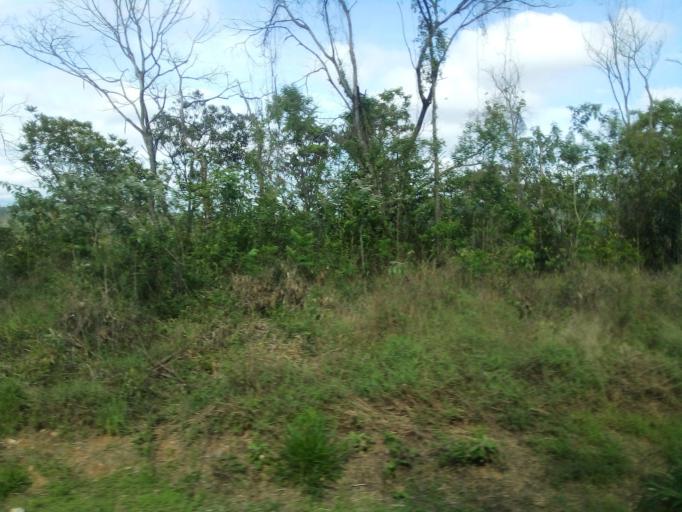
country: BR
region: Minas Gerais
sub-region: Caete
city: Caete
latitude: -19.8782
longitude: -43.7649
